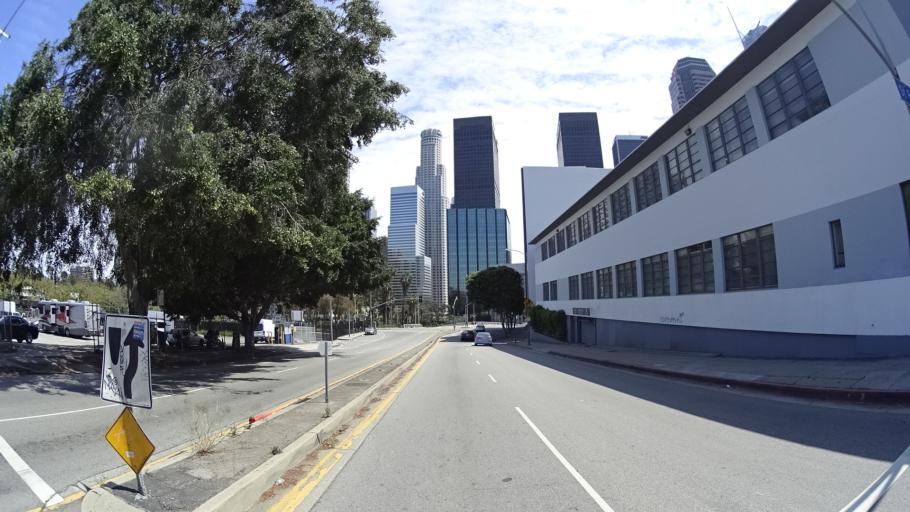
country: US
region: California
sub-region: Los Angeles County
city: Los Angeles
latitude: 34.0535
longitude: -118.2609
